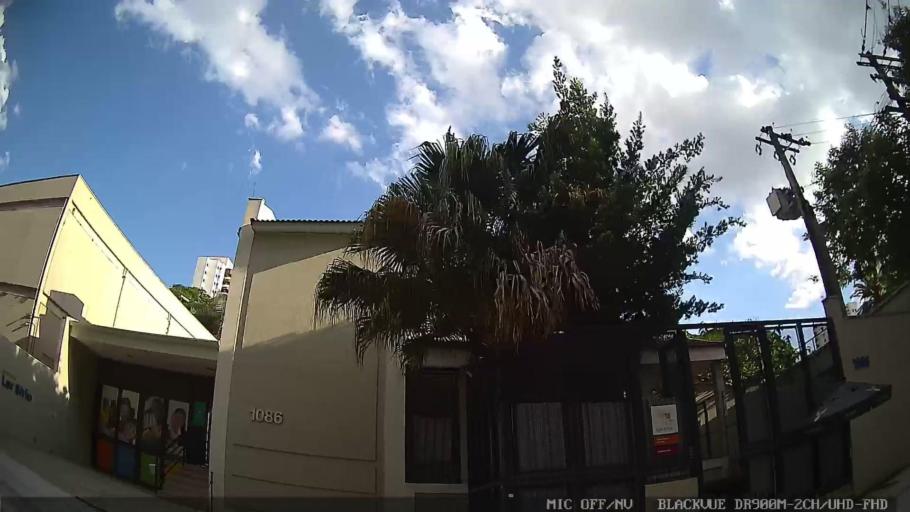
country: BR
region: Sao Paulo
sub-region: Sao Paulo
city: Sao Paulo
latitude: -23.5445
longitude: -46.5655
